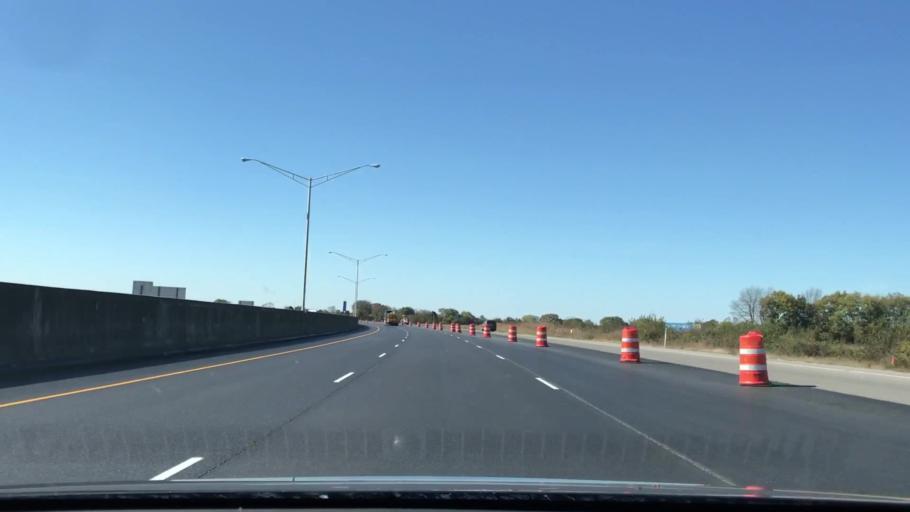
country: US
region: Kentucky
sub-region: Edmonson County
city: Brownsville
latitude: 37.0423
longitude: -86.2142
